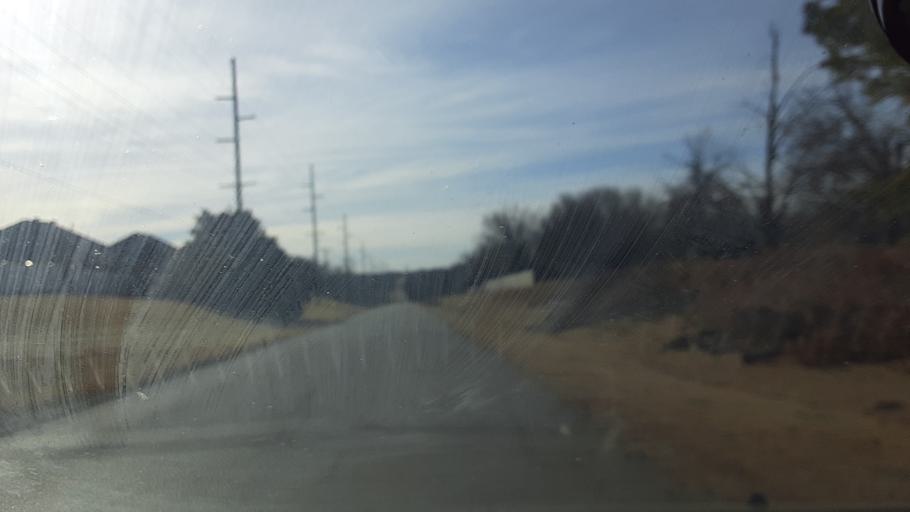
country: US
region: Oklahoma
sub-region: Logan County
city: Guthrie
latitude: 35.8917
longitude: -97.4075
